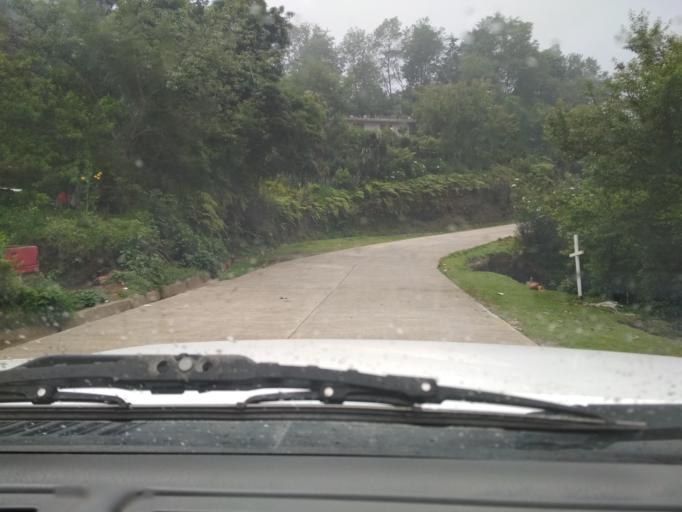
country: MX
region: Veracruz
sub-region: La Perla
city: Barrio de San Miguel
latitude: 18.9560
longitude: -97.1253
